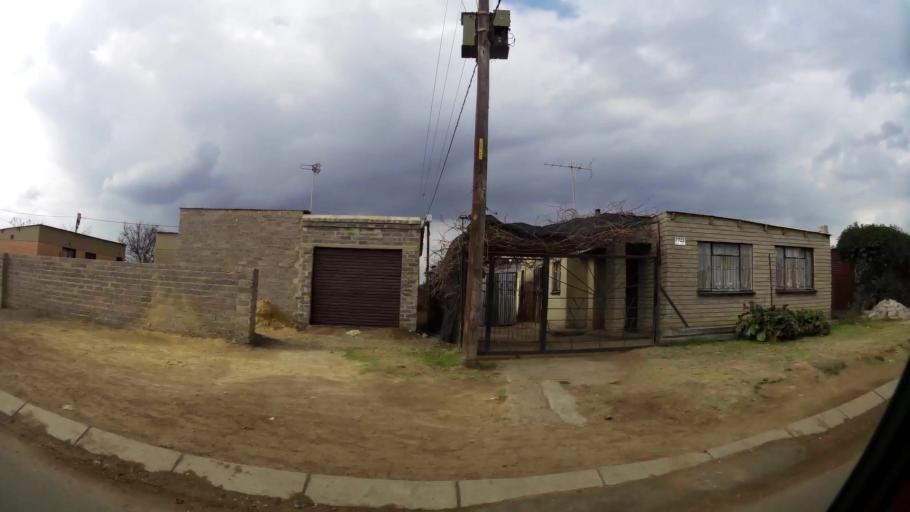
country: ZA
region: Gauteng
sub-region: Sedibeng District Municipality
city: Vanderbijlpark
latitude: -26.6858
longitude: 27.7797
